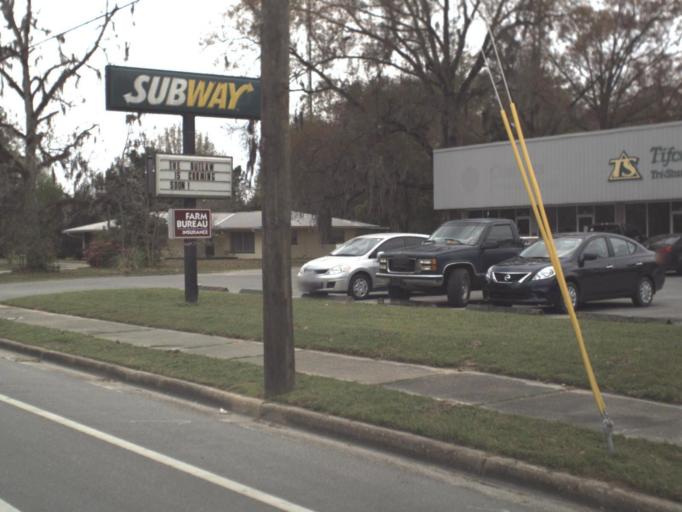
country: US
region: Florida
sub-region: Gulf County
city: Wewahitchka
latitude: 30.1095
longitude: -85.2004
